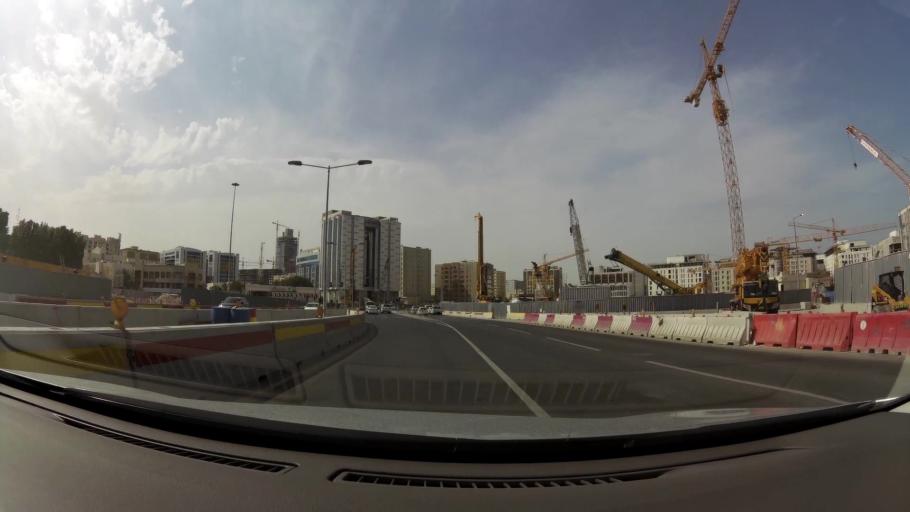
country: QA
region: Baladiyat ad Dawhah
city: Doha
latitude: 25.2816
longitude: 51.5256
